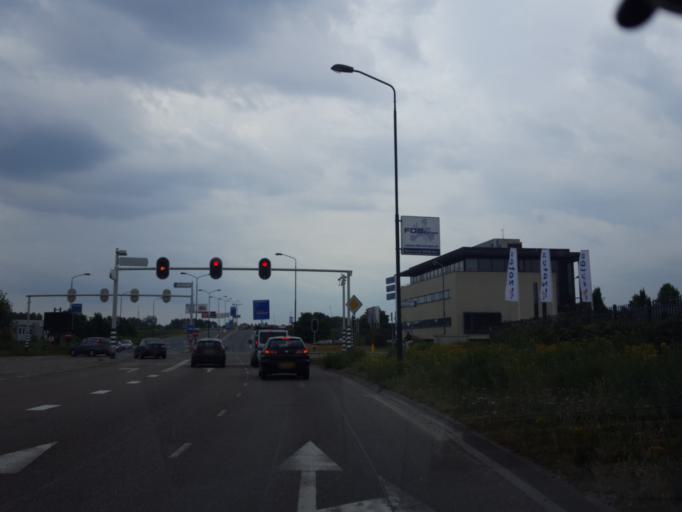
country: NL
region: North Brabant
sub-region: Gemeente Son en Breugel
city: Son
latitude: 51.4998
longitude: 5.4631
